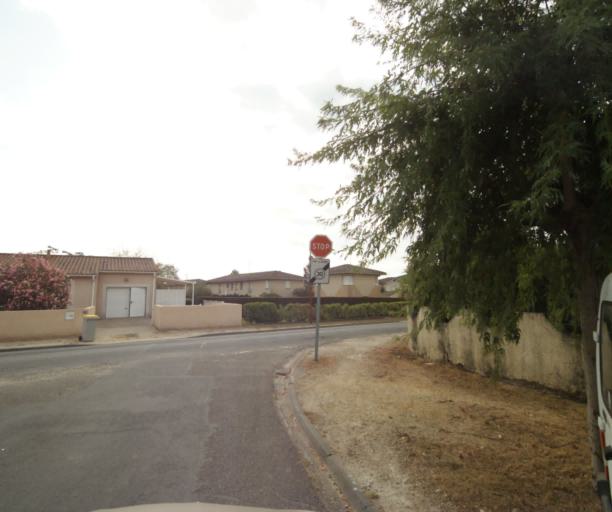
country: FR
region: Aquitaine
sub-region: Departement de la Gironde
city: Creon
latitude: 44.7692
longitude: -0.3441
